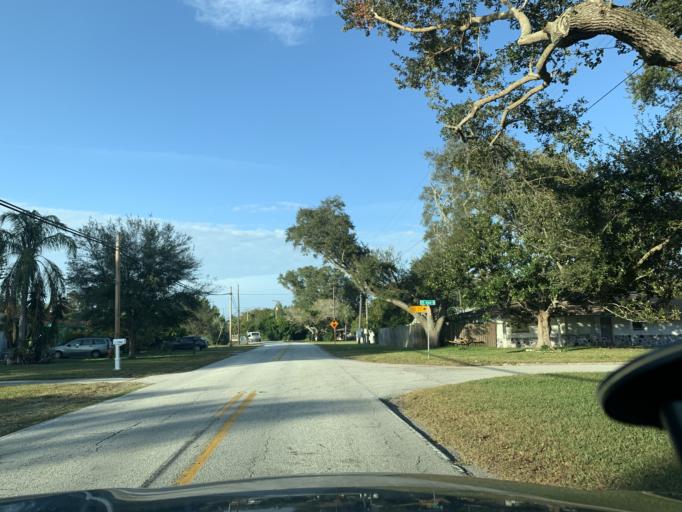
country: US
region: Florida
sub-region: Pinellas County
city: Ridgecrest
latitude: 27.8777
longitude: -82.7974
